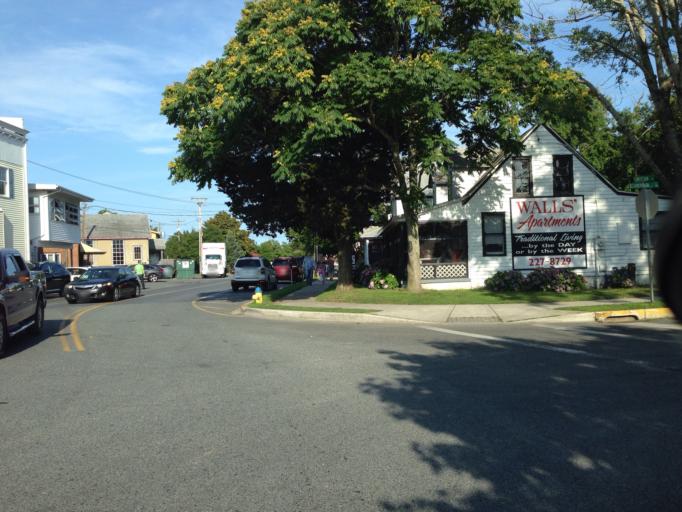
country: US
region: Delaware
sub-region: Sussex County
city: Rehoboth Beach
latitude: 38.7154
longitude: -75.0849
